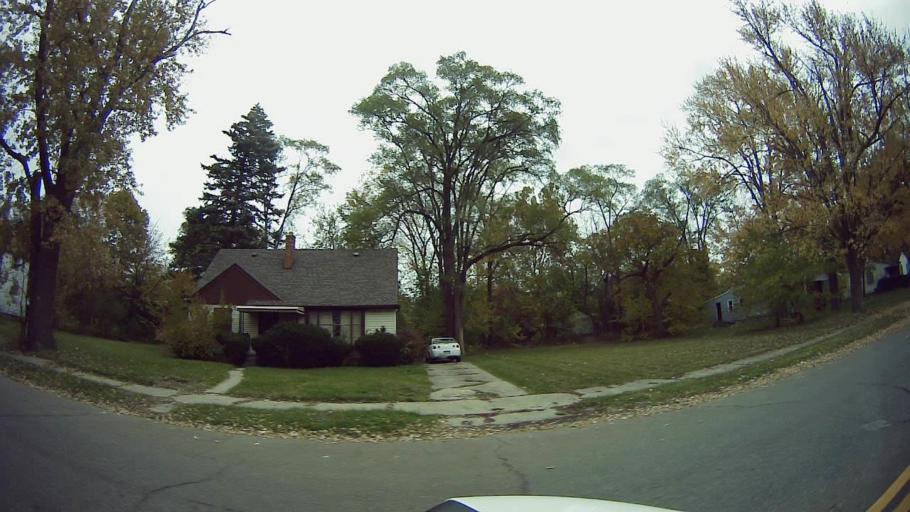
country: US
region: Michigan
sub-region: Oakland County
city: Oak Park
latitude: 42.4046
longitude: -83.1891
